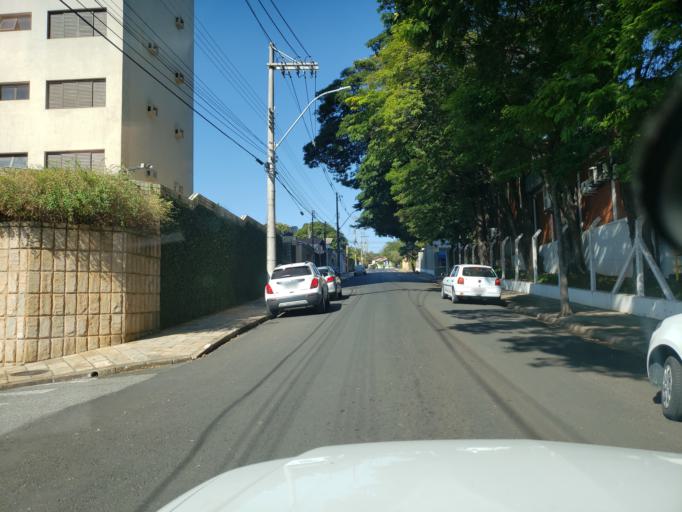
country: BR
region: Sao Paulo
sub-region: Itapira
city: Itapira
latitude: -22.4340
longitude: -46.8336
